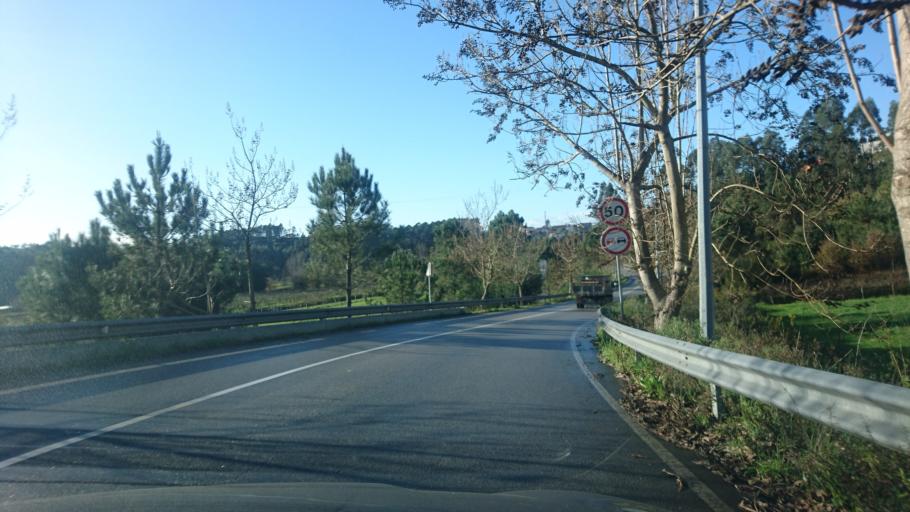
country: PT
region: Porto
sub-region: Paredes
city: Recarei
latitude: 41.1488
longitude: -8.3949
